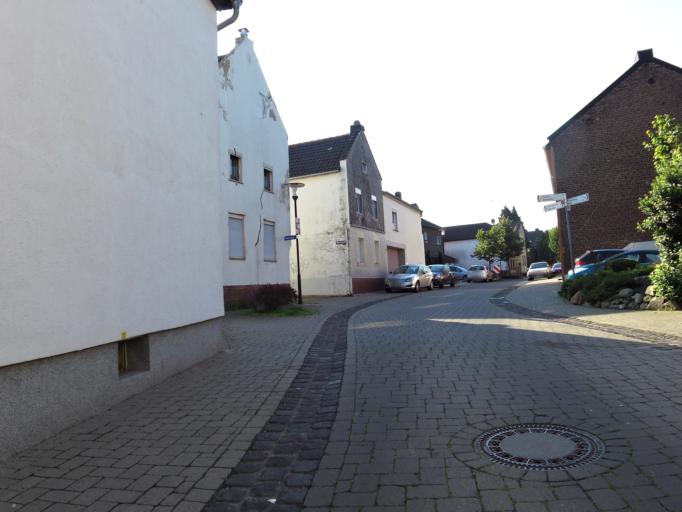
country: DE
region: North Rhine-Westphalia
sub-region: Regierungsbezirk Koln
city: Ubach-Palenberg
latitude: 50.9036
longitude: 6.1358
